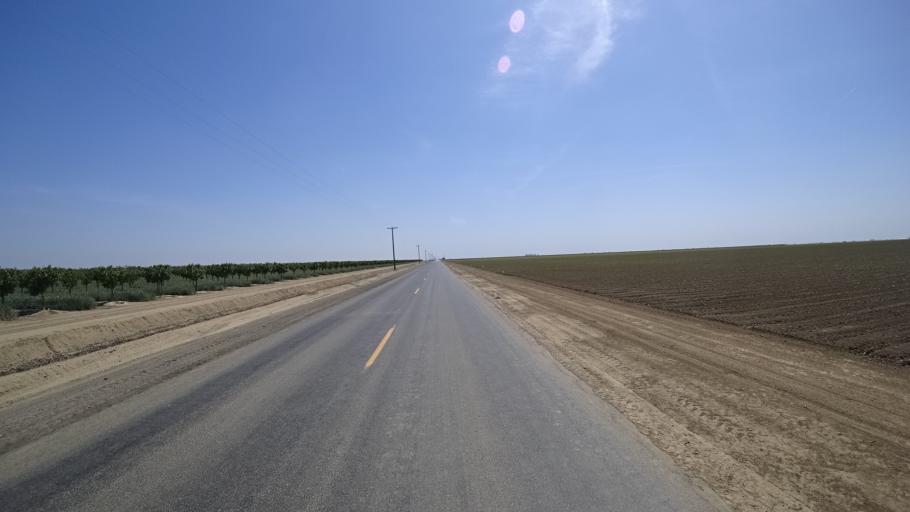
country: US
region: California
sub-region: Kings County
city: Kettleman City
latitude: 36.1377
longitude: -119.9572
